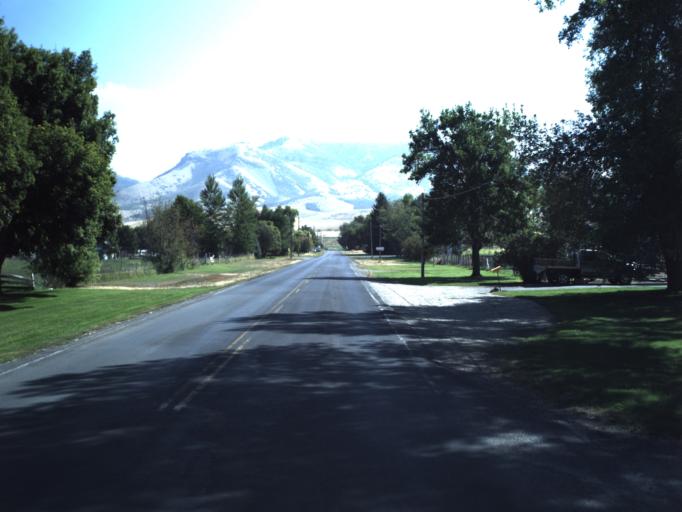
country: US
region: Utah
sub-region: Cache County
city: Hyrum
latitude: 41.5665
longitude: -111.8328
